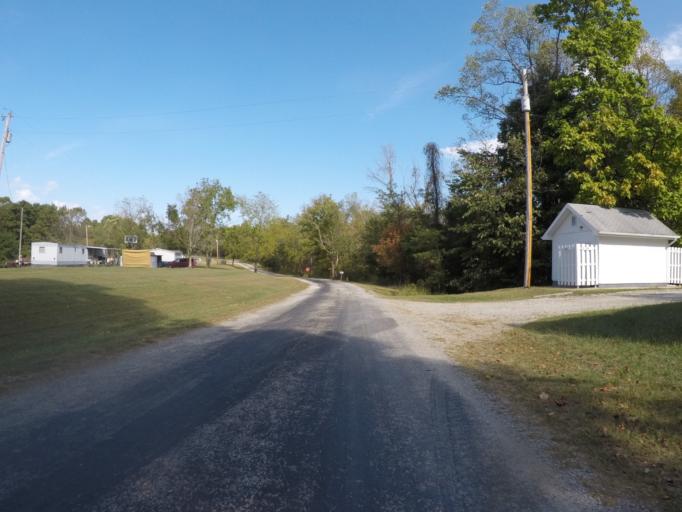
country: US
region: West Virginia
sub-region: Cabell County
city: Lesage
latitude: 38.6407
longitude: -82.4029
